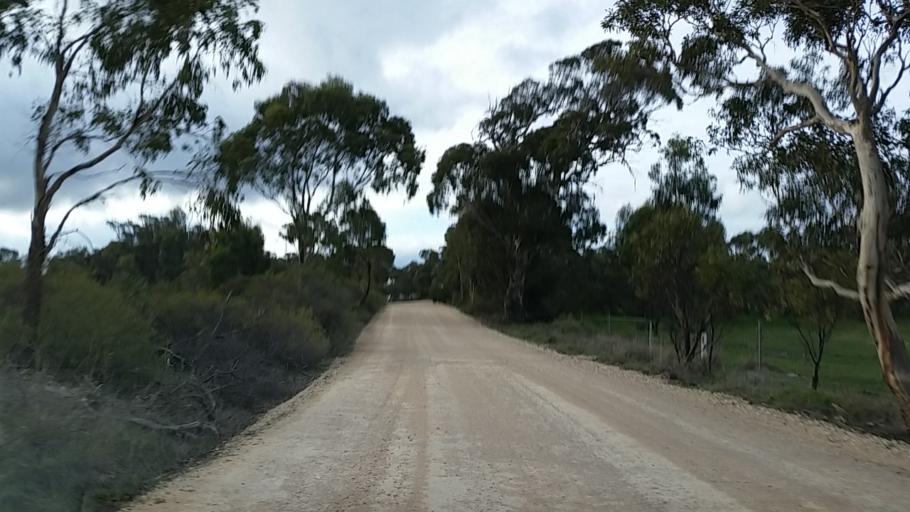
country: AU
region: South Australia
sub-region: Mount Barker
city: Callington
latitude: -34.9876
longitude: 139.0577
